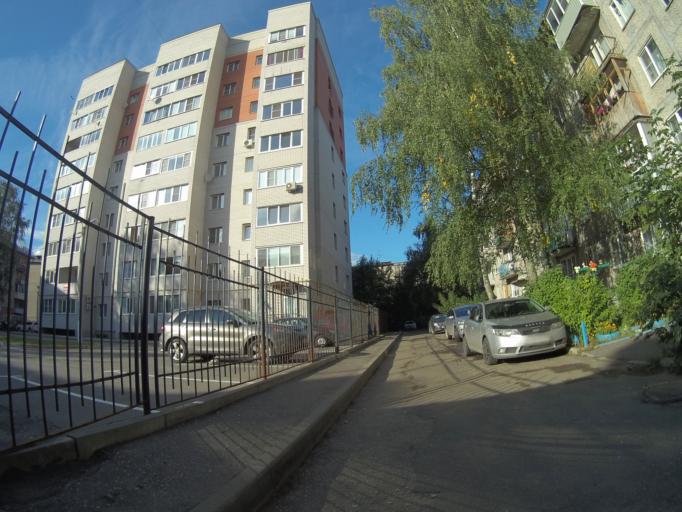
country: RU
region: Vladimir
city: Vladimir
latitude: 56.1507
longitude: 40.3739
